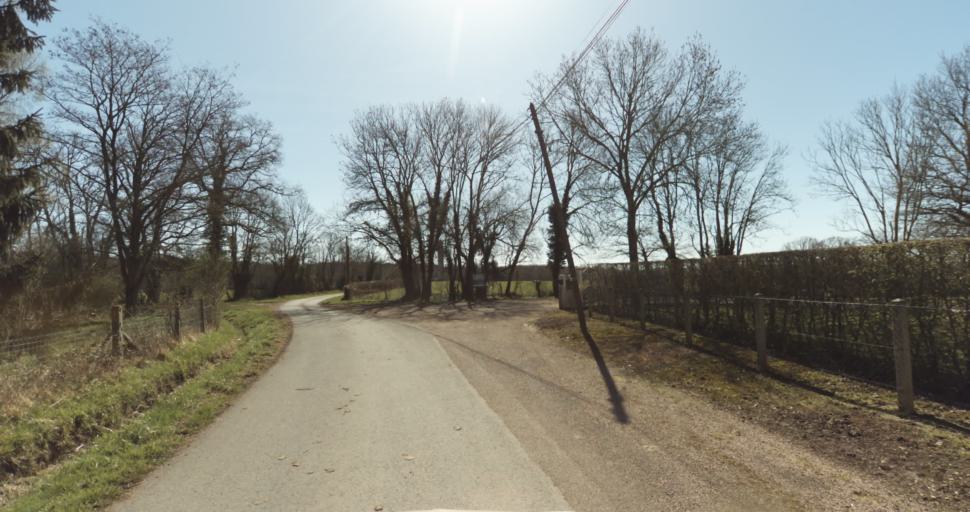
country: FR
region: Lower Normandy
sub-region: Departement du Calvados
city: Livarot
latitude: 48.9659
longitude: 0.0764
